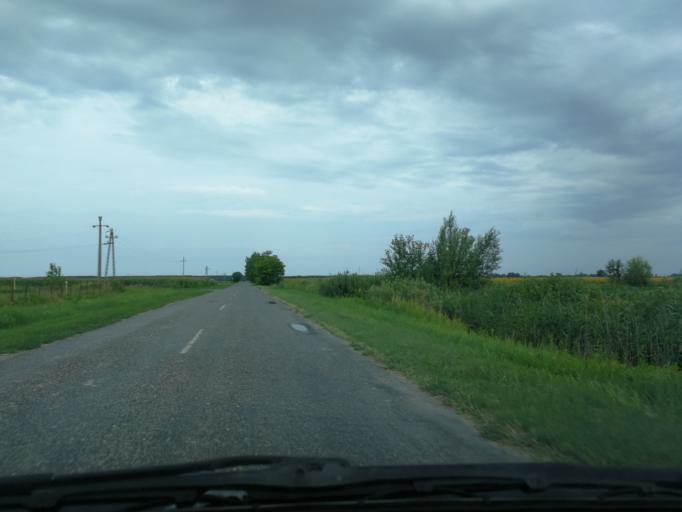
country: HU
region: Bacs-Kiskun
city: Batya
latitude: 46.4487
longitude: 18.9764
